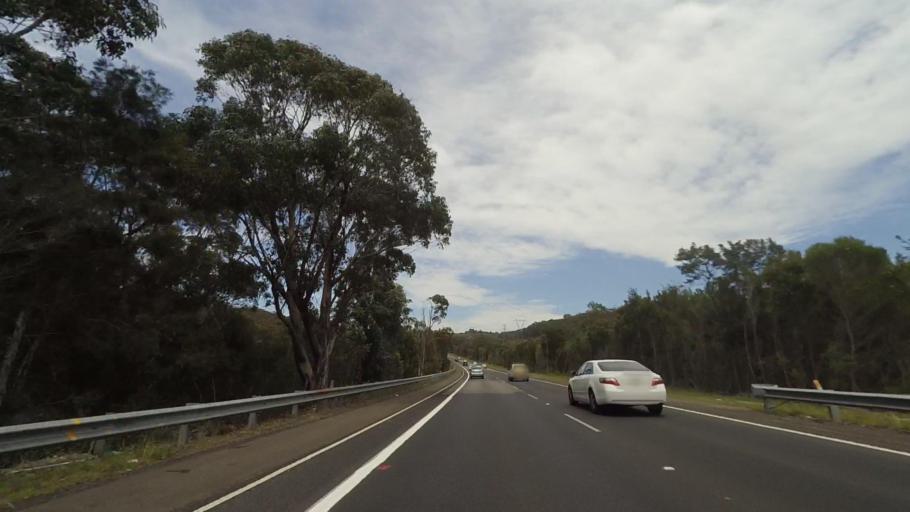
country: AU
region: New South Wales
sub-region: Wollongong
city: Helensburgh
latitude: -34.1622
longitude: 150.9809
